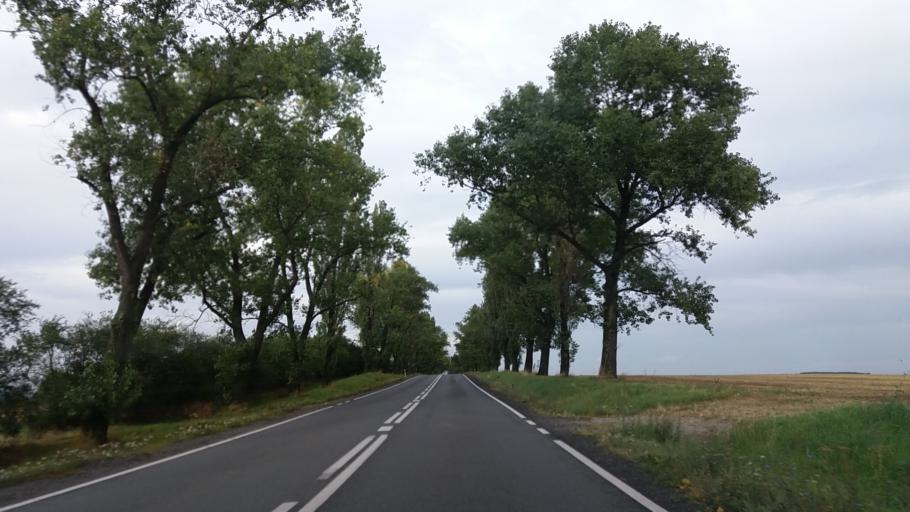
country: PL
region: Lower Silesian Voivodeship
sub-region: Powiat swidnicki
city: Stanowice
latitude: 50.9103
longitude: 16.3637
